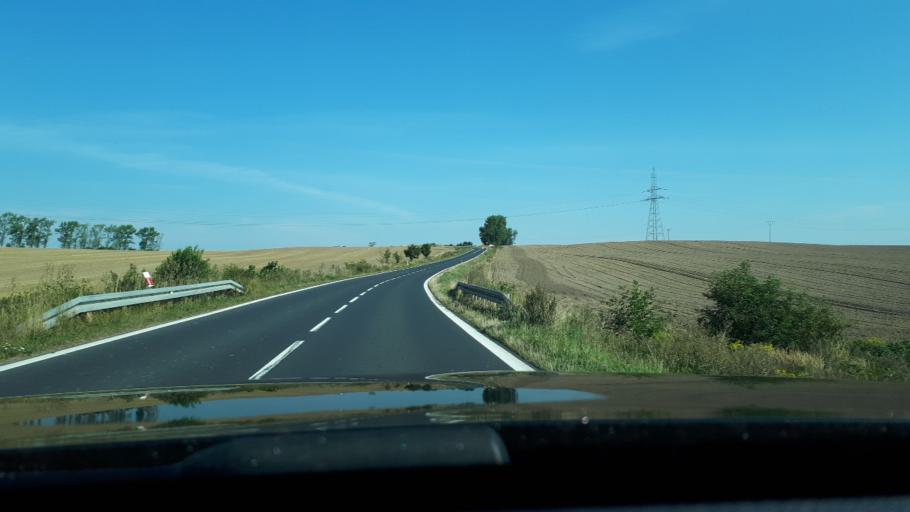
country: PL
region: Lower Silesian Voivodeship
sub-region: Powiat lubanski
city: Pisarzowice
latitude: 51.1752
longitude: 15.2618
